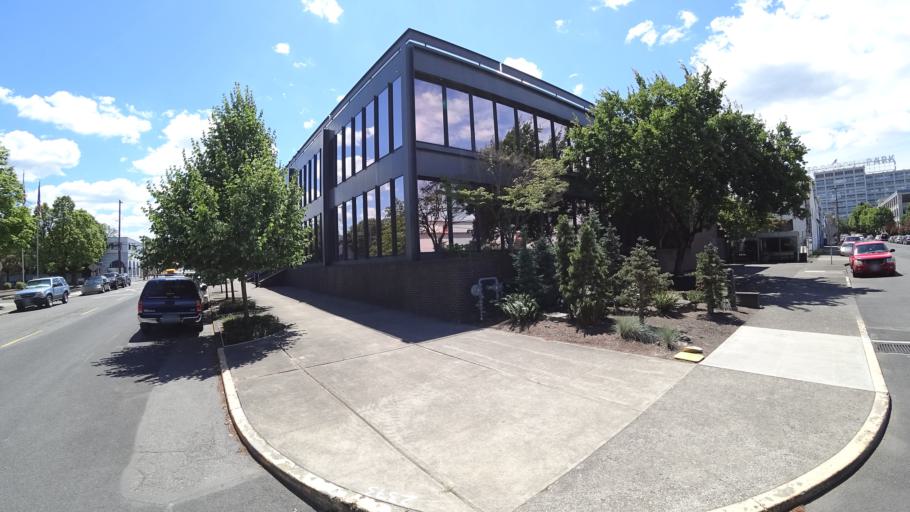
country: US
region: Oregon
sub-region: Multnomah County
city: Portland
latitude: 45.5375
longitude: -122.7030
